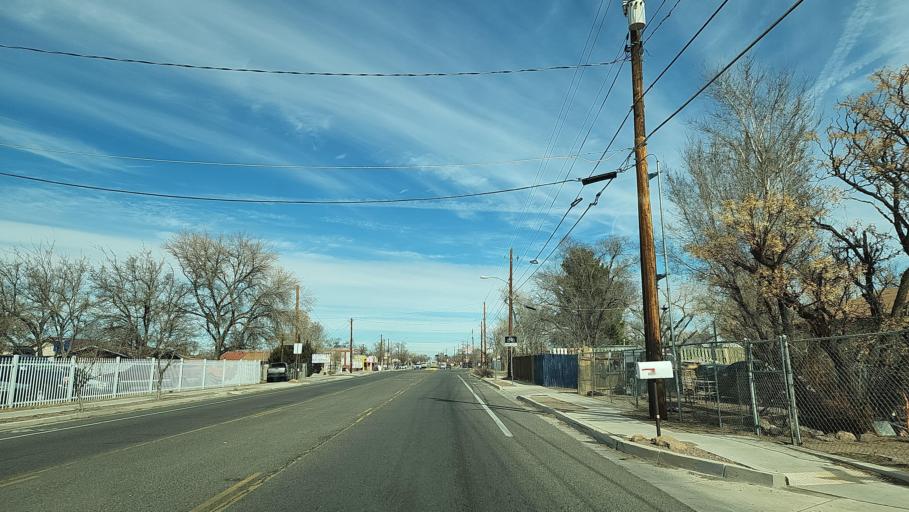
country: US
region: New Mexico
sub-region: Bernalillo County
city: South Valley
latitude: 35.0359
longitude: -106.6794
